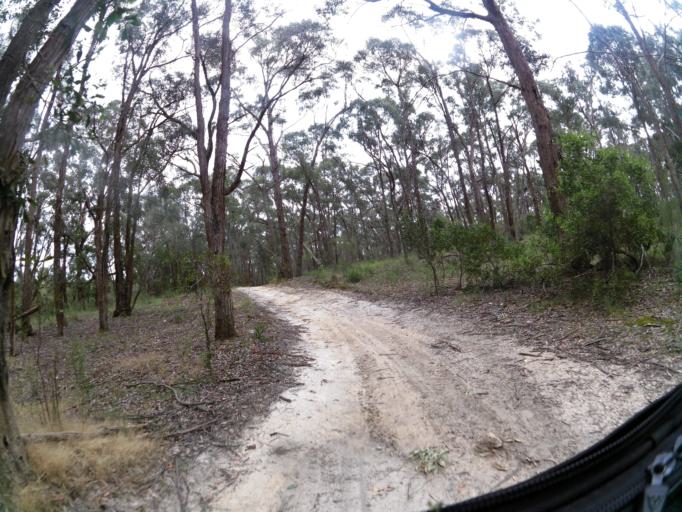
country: AU
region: Victoria
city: Brown Hill
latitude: -37.4559
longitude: 143.9098
